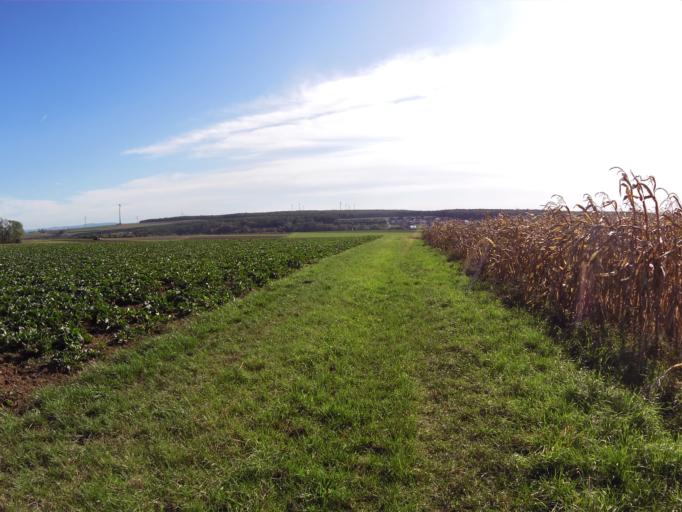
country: DE
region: Bavaria
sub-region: Regierungsbezirk Unterfranken
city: Theilheim
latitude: 49.7642
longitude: 10.0201
